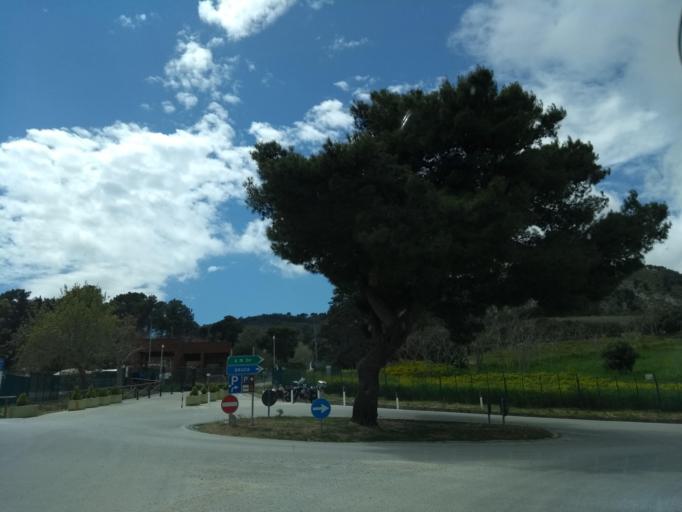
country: IT
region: Sicily
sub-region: Trapani
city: Calatafimi
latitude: 37.9422
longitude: 12.8364
